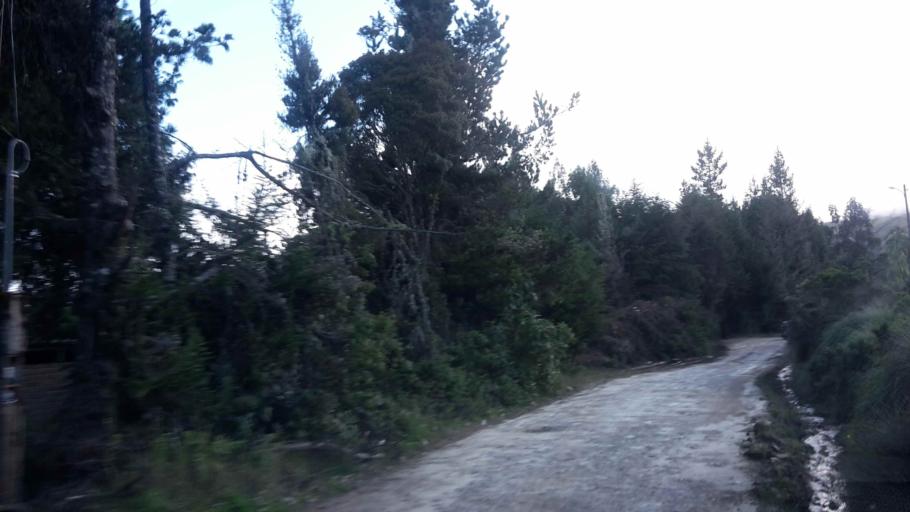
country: BO
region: Cochabamba
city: Colomi
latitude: -17.2370
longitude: -65.9005
